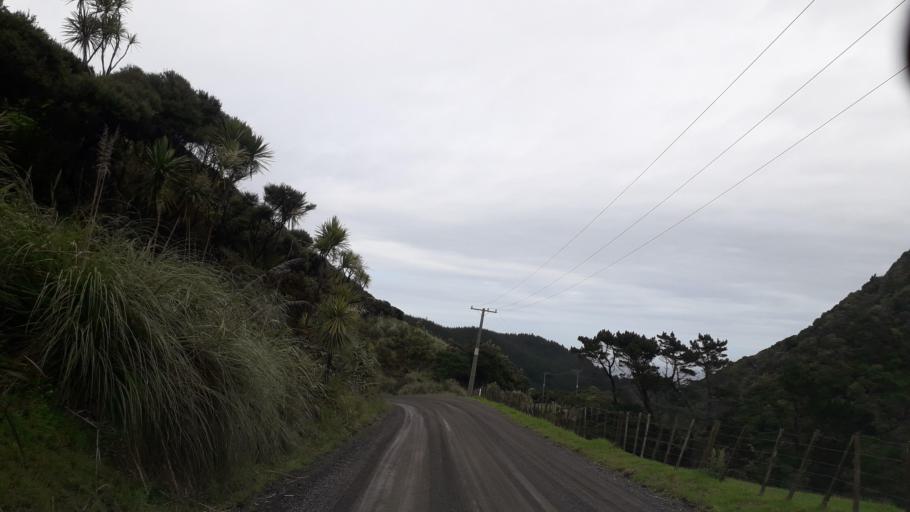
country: NZ
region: Northland
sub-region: Far North District
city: Ahipara
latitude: -35.4369
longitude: 173.3066
